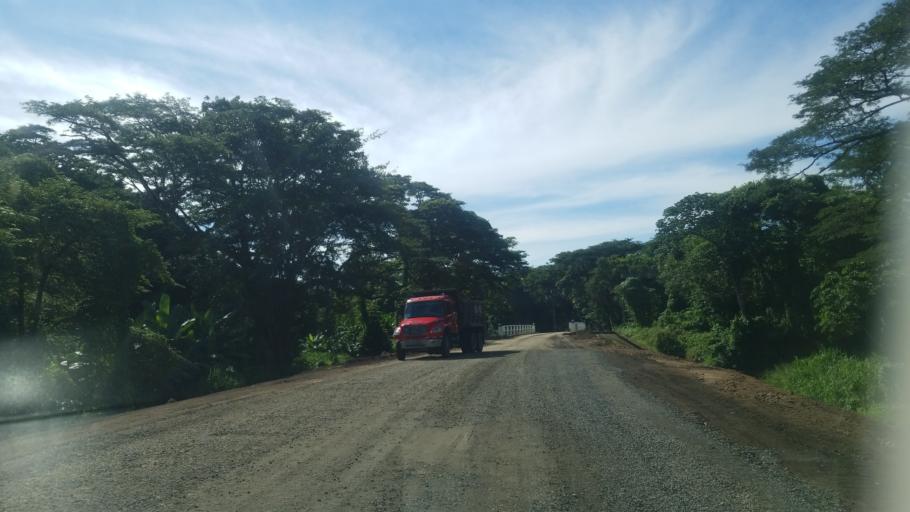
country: NI
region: Rivas
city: Cardenas
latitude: 11.1294
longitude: -85.3114
